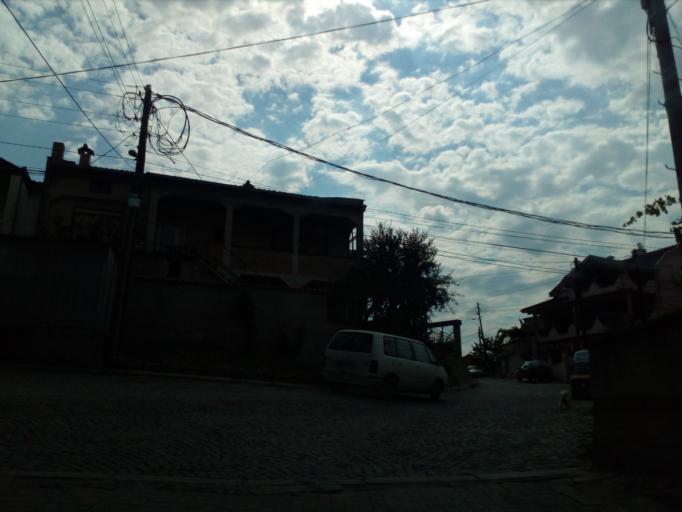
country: MK
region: Veles
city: Veles
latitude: 41.7135
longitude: 21.7779
